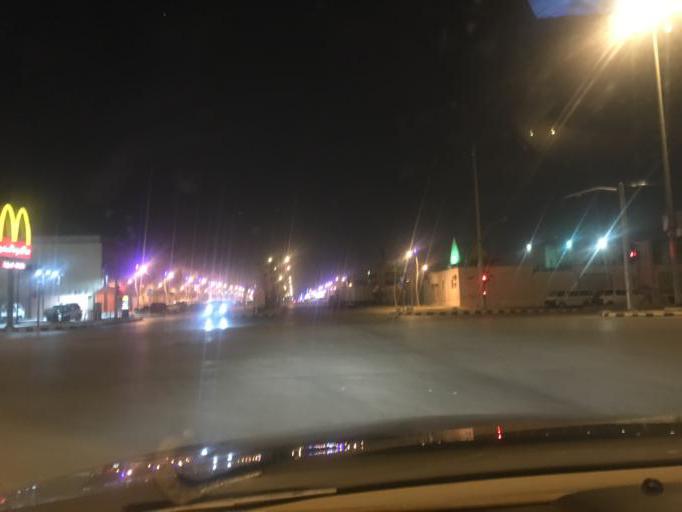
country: SA
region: Ar Riyad
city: Riyadh
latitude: 24.7620
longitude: 46.7981
